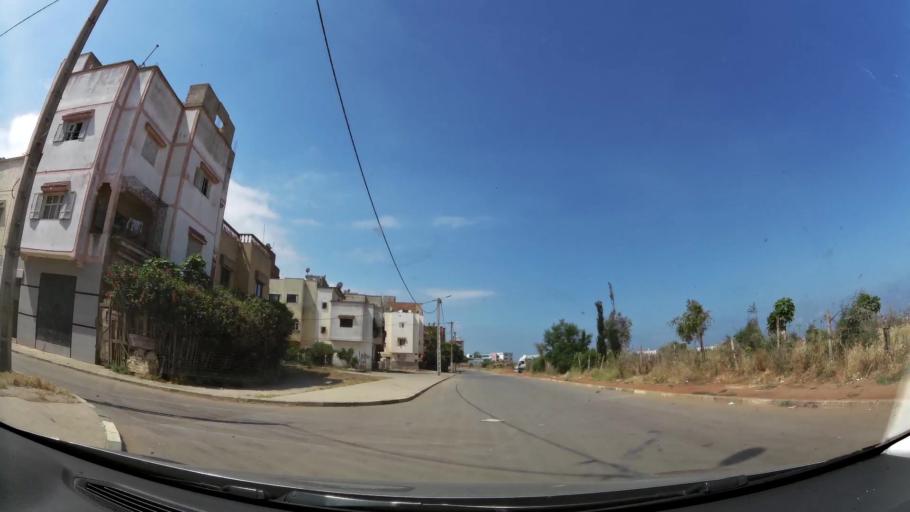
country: MA
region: Rabat-Sale-Zemmour-Zaer
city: Sale
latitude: 34.0666
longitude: -6.7832
